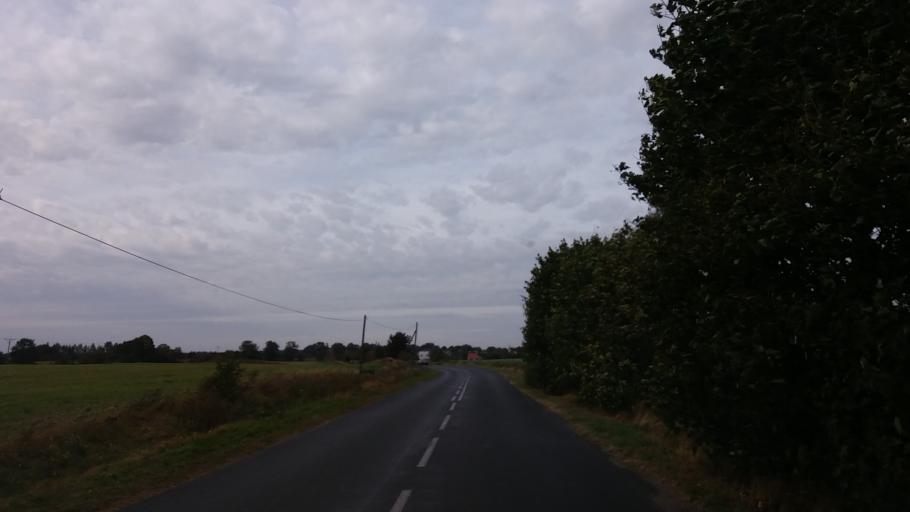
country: PL
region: Lubusz
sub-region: Powiat strzelecko-drezdenecki
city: Strzelce Krajenskie
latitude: 52.9176
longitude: 15.4910
